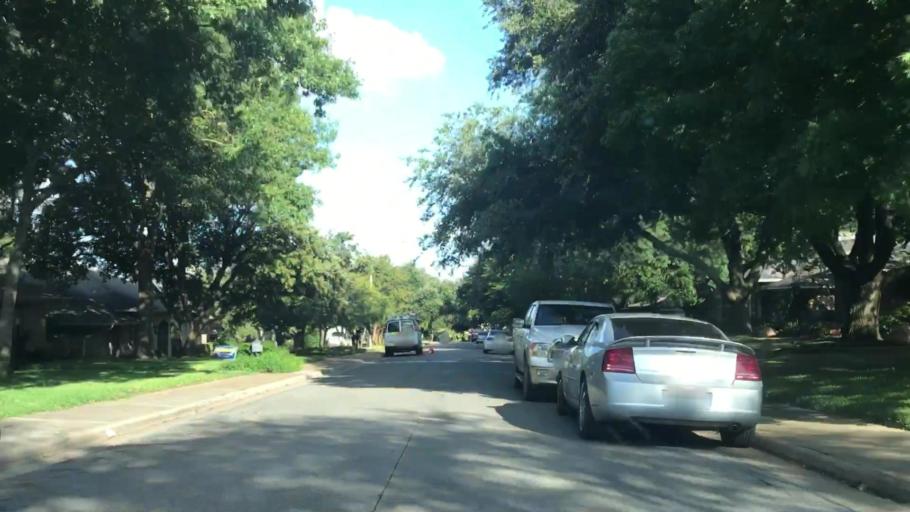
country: US
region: Texas
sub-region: Dallas County
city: Highland Park
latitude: 32.8283
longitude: -96.7507
